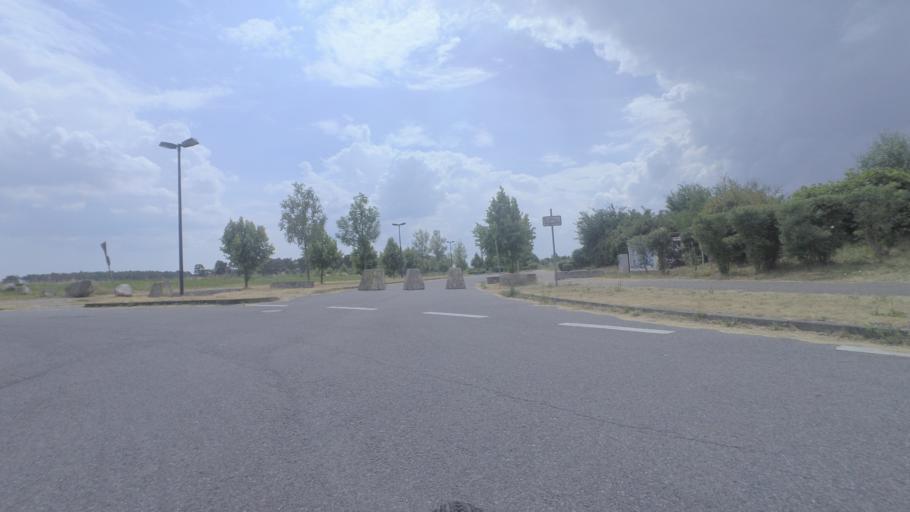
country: DE
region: Brandenburg
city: Grossbeeren
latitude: 52.3243
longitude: 13.2923
